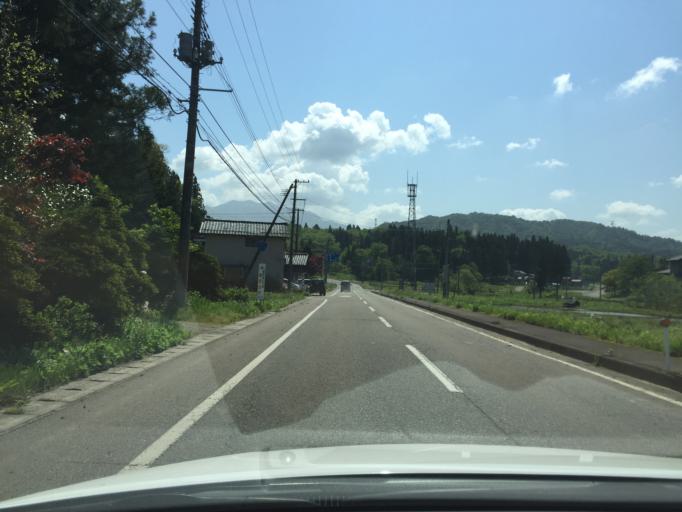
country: JP
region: Niigata
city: Kamo
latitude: 37.5762
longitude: 139.0854
